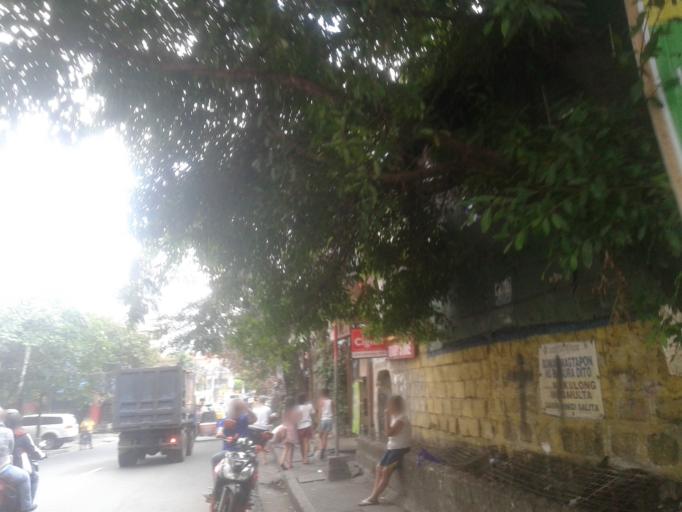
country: PH
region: Metro Manila
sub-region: Mandaluyong
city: Mandaluyong City
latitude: 14.5864
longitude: 121.0436
